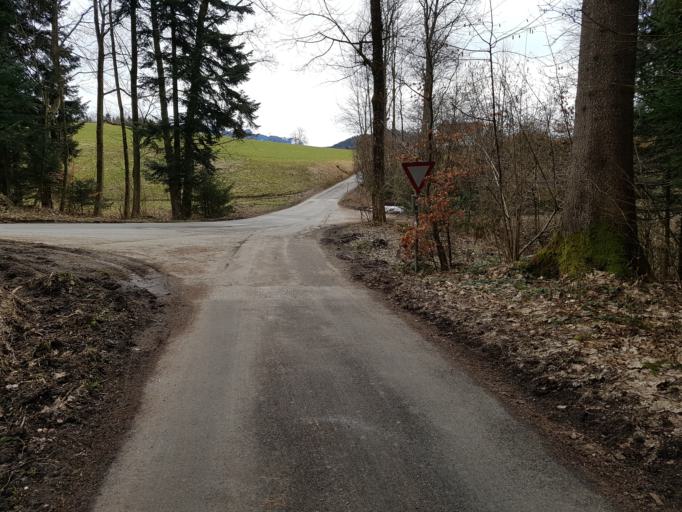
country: AT
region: Salzburg
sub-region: Politischer Bezirk Hallein
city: Adnet
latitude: 47.6740
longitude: 13.1381
